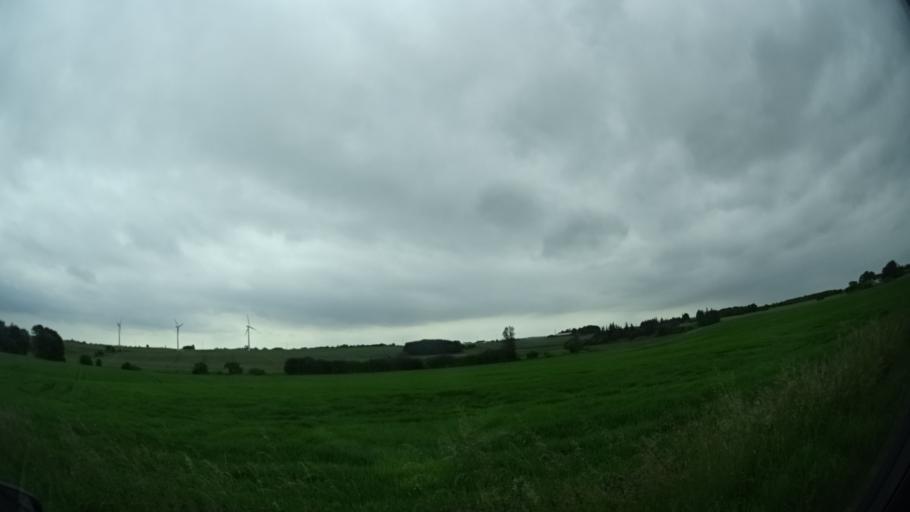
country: DK
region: Central Jutland
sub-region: Arhus Kommune
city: Solbjerg
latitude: 56.0765
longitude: 10.0878
